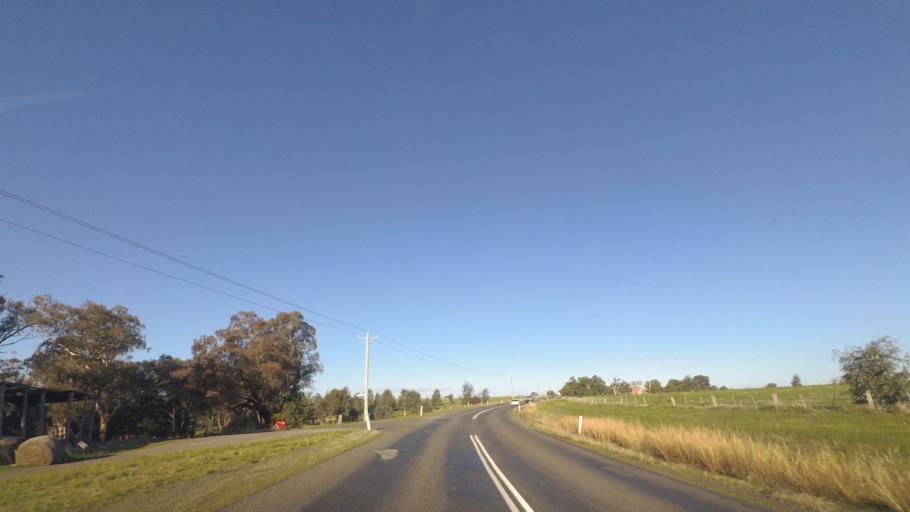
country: AU
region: Victoria
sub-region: Greater Bendigo
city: Kennington
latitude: -36.8155
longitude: 144.5123
